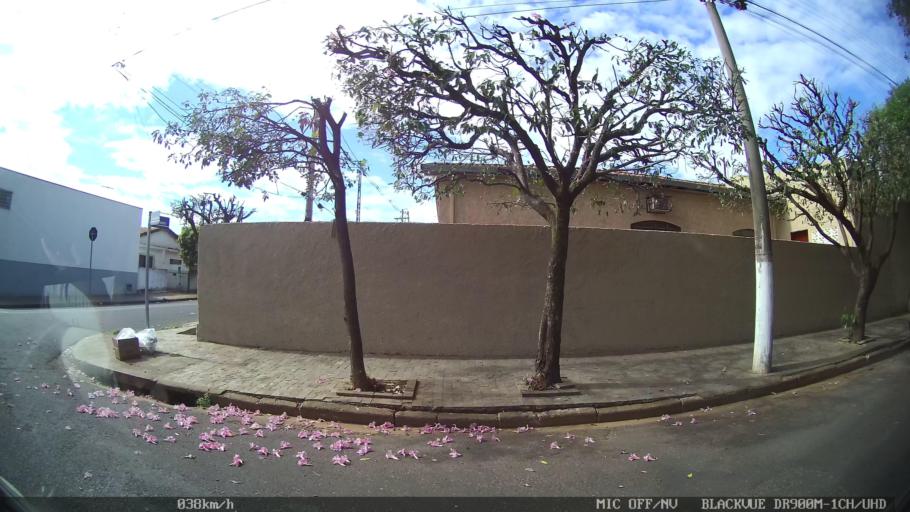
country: BR
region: Sao Paulo
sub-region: Bady Bassitt
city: Bady Bassitt
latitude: -20.8164
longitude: -49.5231
